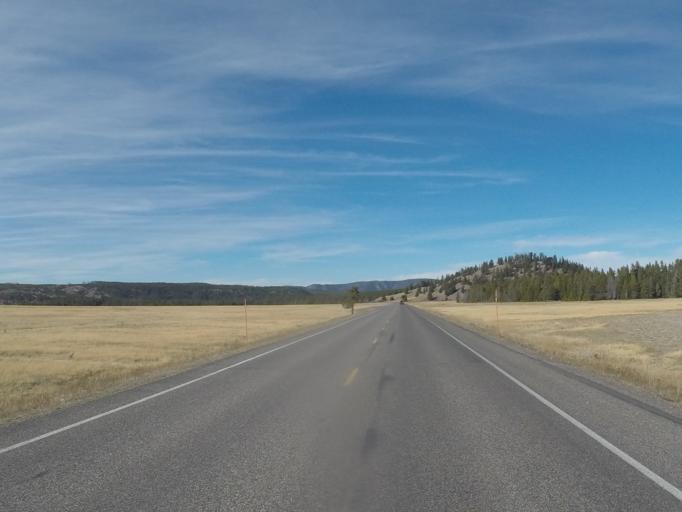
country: US
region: Montana
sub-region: Gallatin County
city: West Yellowstone
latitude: 44.5628
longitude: -110.8111
